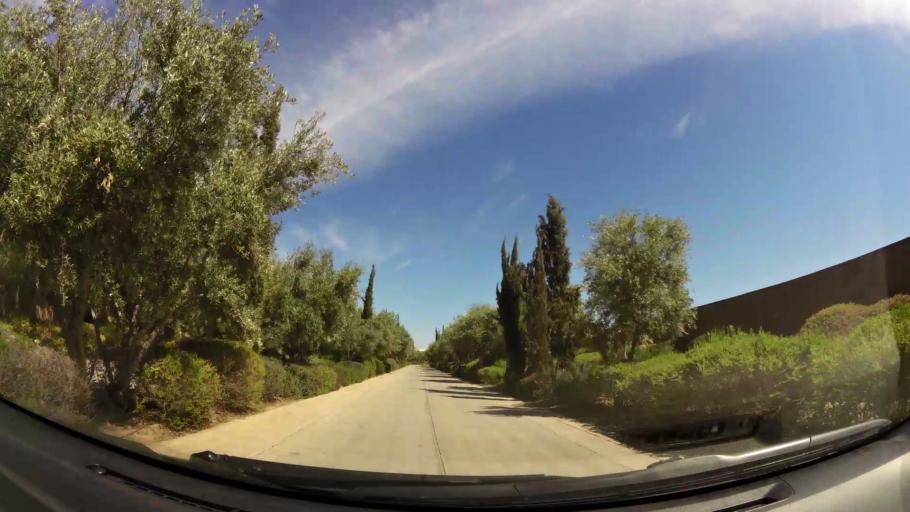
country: MA
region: Marrakech-Tensift-Al Haouz
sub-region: Marrakech
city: Marrakesh
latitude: 31.6020
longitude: -7.9530
